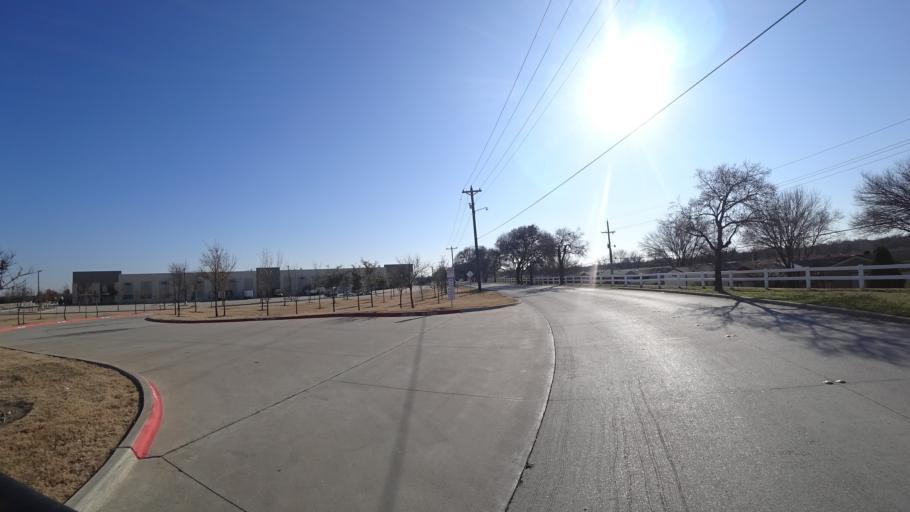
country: US
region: Texas
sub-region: Dallas County
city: Coppell
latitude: 32.9948
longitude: -97.0158
